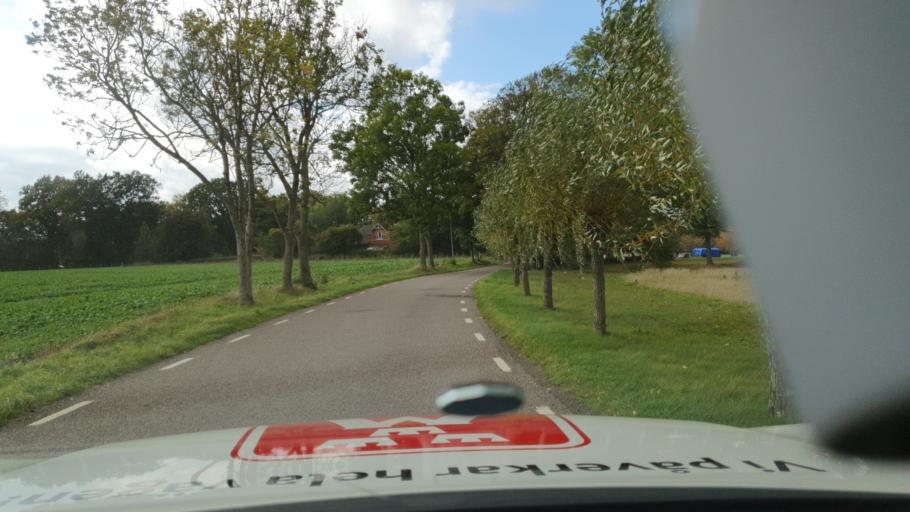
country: SE
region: Skane
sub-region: Trelleborgs Kommun
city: Trelleborg
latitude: 55.4401
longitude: 13.1278
